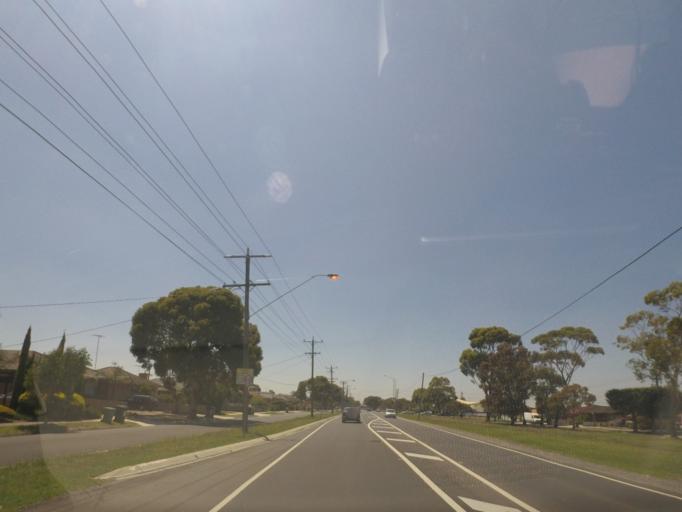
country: AU
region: Victoria
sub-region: Hume
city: Craigieburn
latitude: -37.5975
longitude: 144.9286
